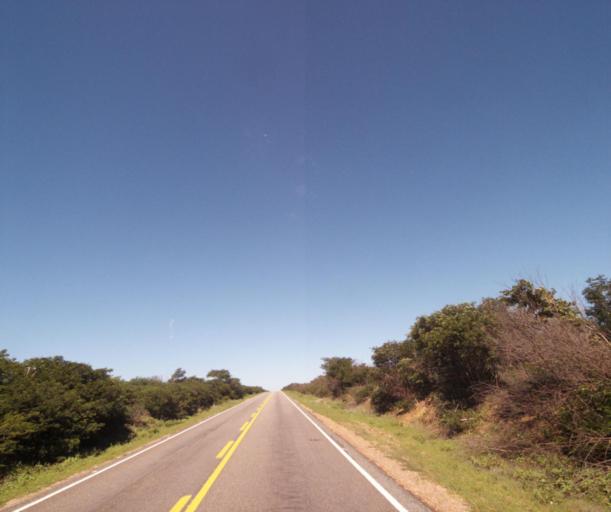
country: BR
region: Bahia
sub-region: Palmas De Monte Alto
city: Palmas de Monte Alto
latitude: -14.2532
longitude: -43.2084
